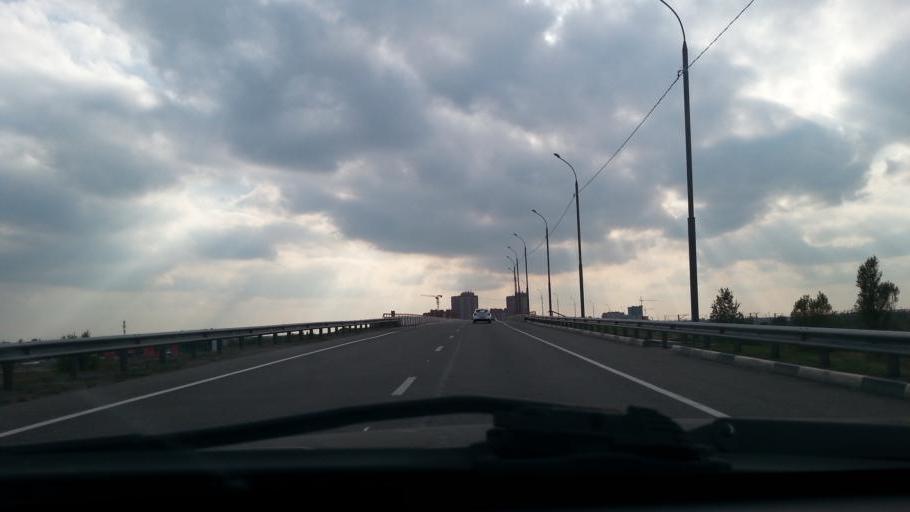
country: RU
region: Rostov
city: Bataysk
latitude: 47.1607
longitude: 39.7385
